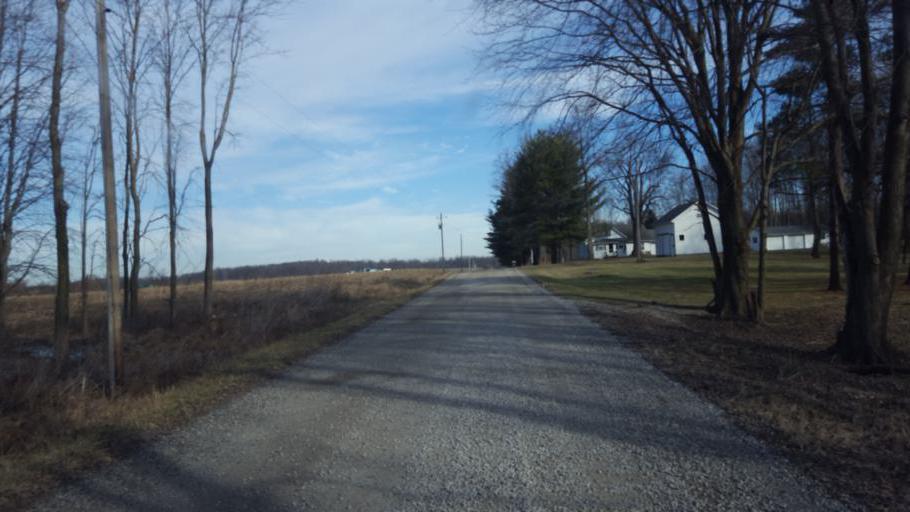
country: US
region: Ohio
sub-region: Morrow County
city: Mount Gilead
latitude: 40.5529
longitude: -82.7104
